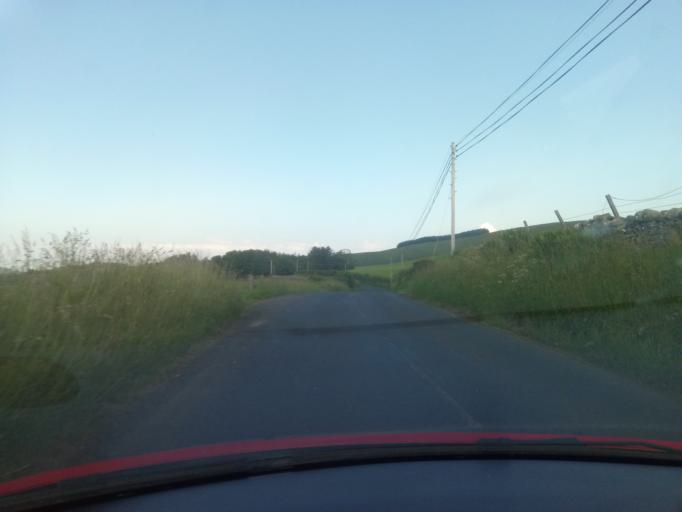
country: GB
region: Scotland
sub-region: The Scottish Borders
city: Selkirk
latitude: 55.5103
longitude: -2.9462
